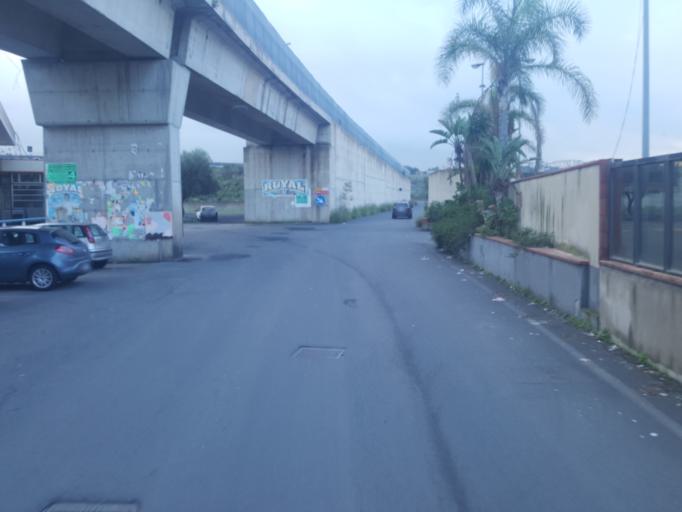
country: IT
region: Sicily
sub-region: Catania
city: Belvedere-Piano Tavola
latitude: 37.5377
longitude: 14.9708
